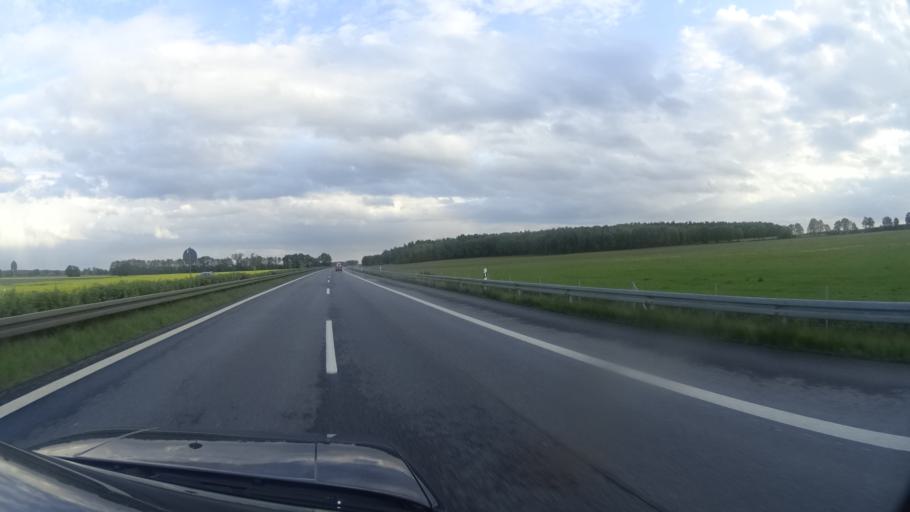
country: DE
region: Brandenburg
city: Wittstock
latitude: 53.2351
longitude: 12.4500
